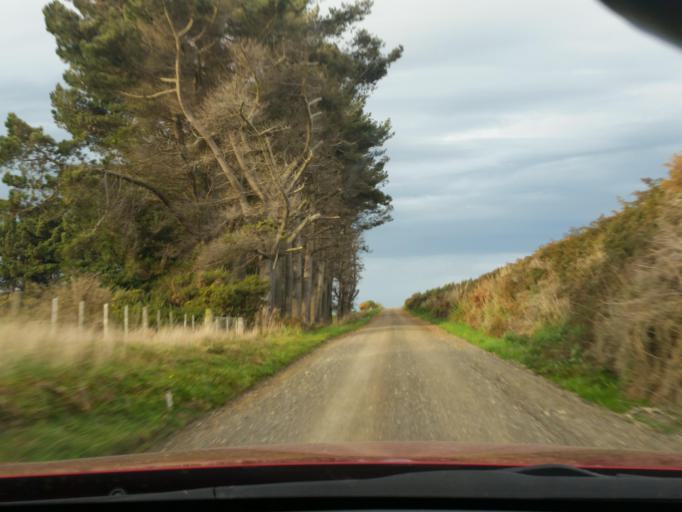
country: NZ
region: Southland
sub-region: Southland District
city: Riverton
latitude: -46.3418
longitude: 167.9318
